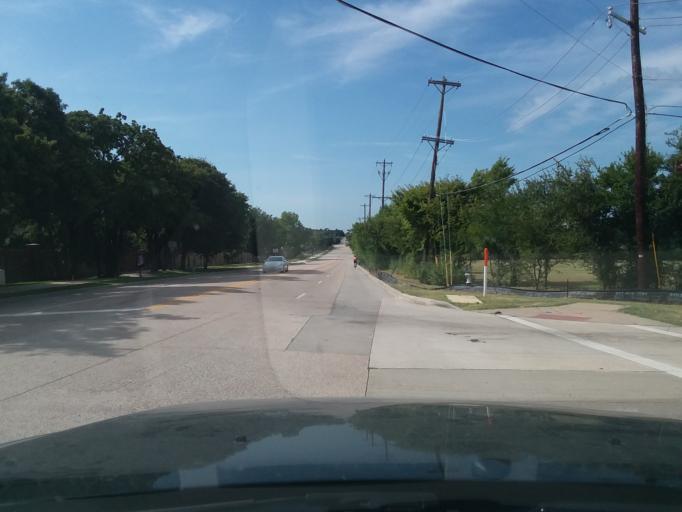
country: US
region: Texas
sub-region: Denton County
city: Flower Mound
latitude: 33.0213
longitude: -97.0884
